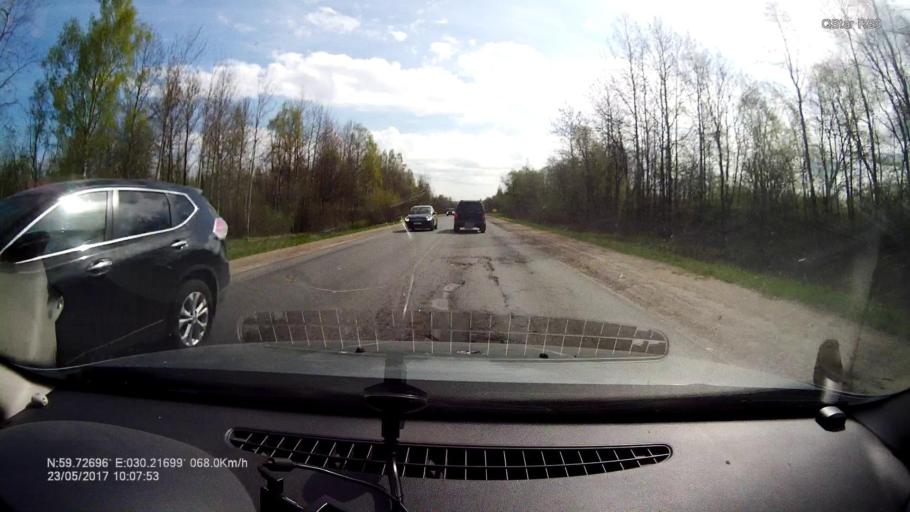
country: RU
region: St.-Petersburg
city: Gorelovo
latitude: 59.7270
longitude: 30.2170
